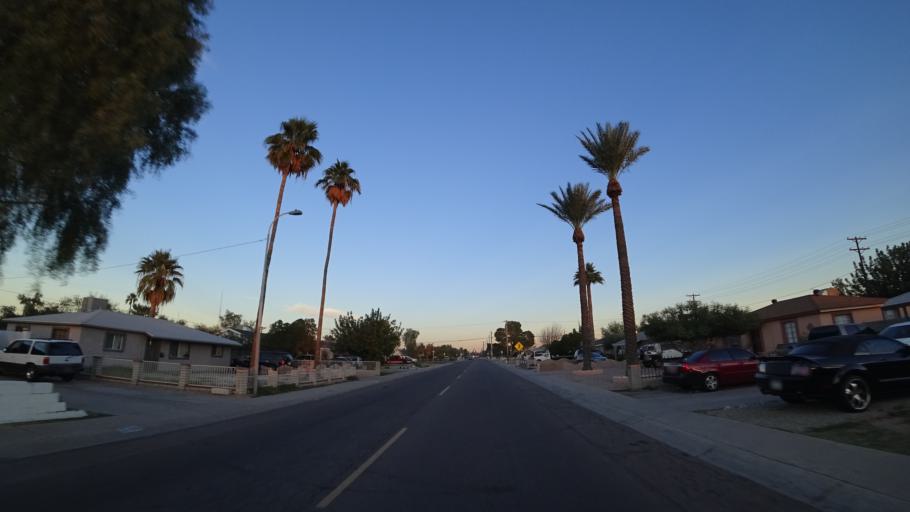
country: US
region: Arizona
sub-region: Maricopa County
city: Phoenix
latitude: 33.4731
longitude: -112.0099
